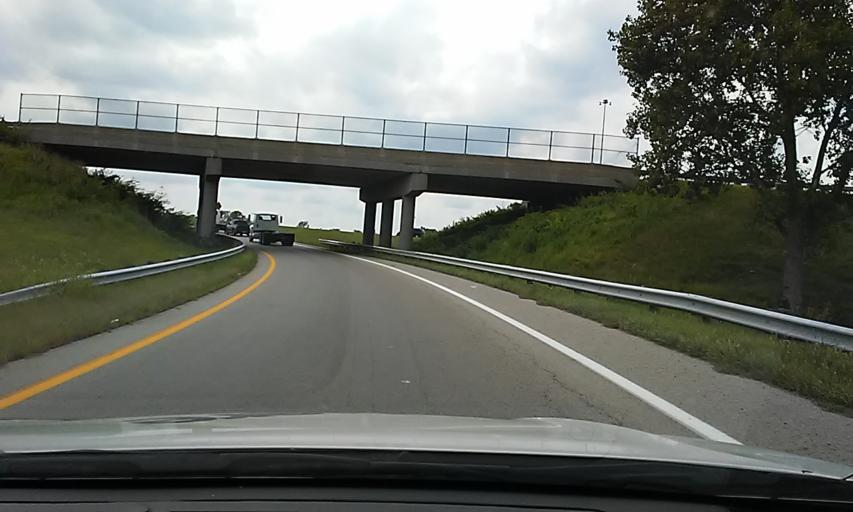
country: US
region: Ohio
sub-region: Clark County
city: Park Layne
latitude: 39.8674
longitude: -84.0547
